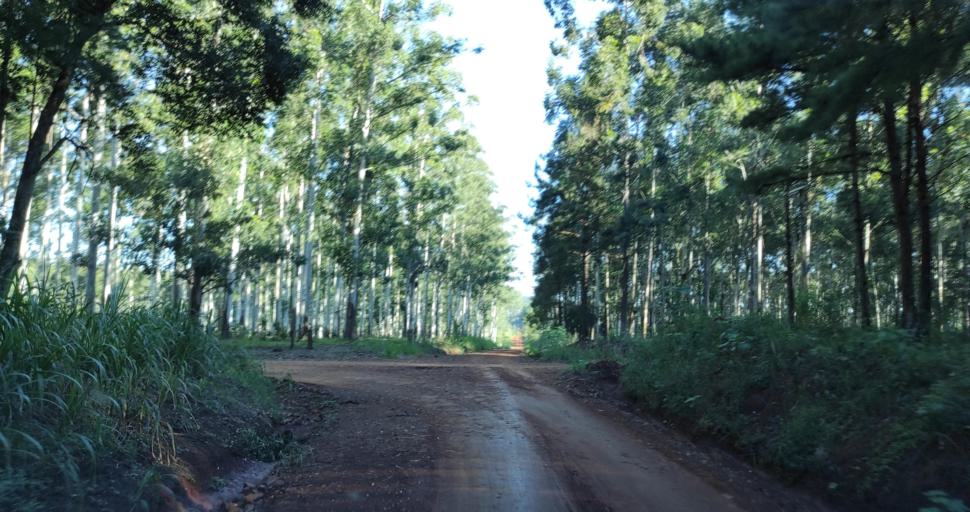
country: AR
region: Misiones
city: Puerto Rico
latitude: -26.8615
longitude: -55.0148
